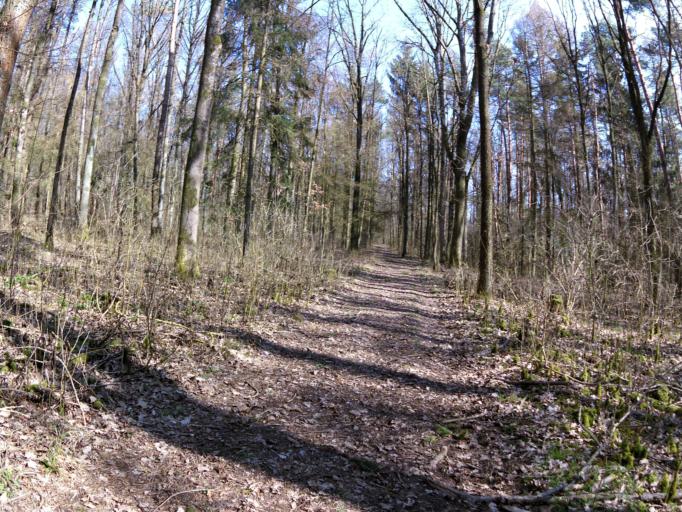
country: DE
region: Bavaria
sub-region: Regierungsbezirk Unterfranken
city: Rottendorf
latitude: 49.8070
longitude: 10.0145
